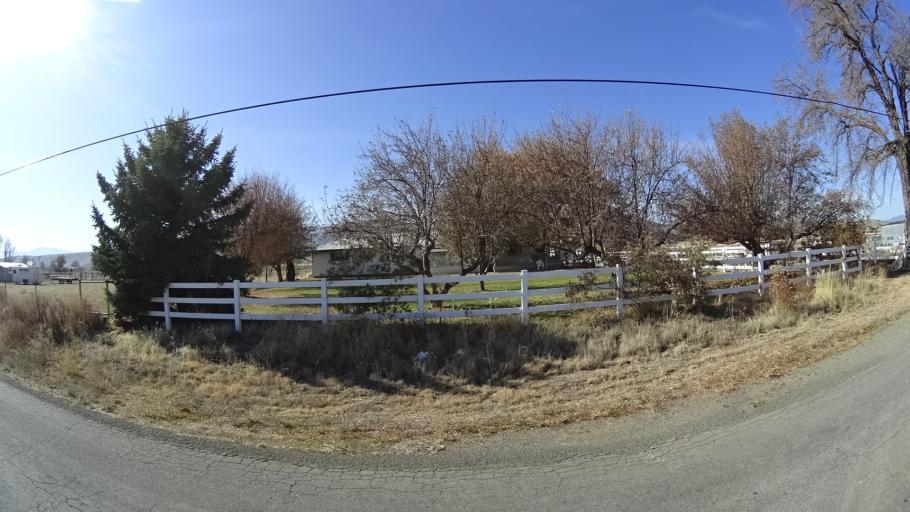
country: US
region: California
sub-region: Siskiyou County
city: Montague
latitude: 41.6204
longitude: -122.5225
